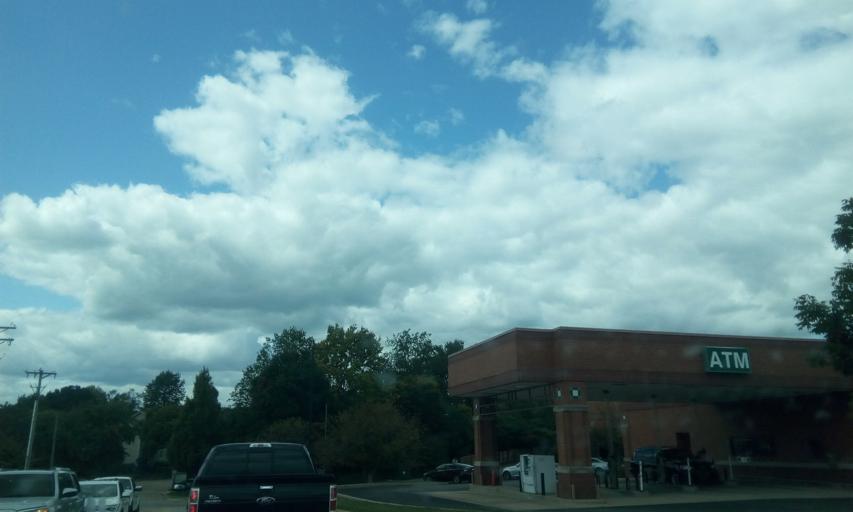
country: US
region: Missouri
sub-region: Saint Louis County
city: Chesterfield
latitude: 38.6438
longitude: -90.5663
